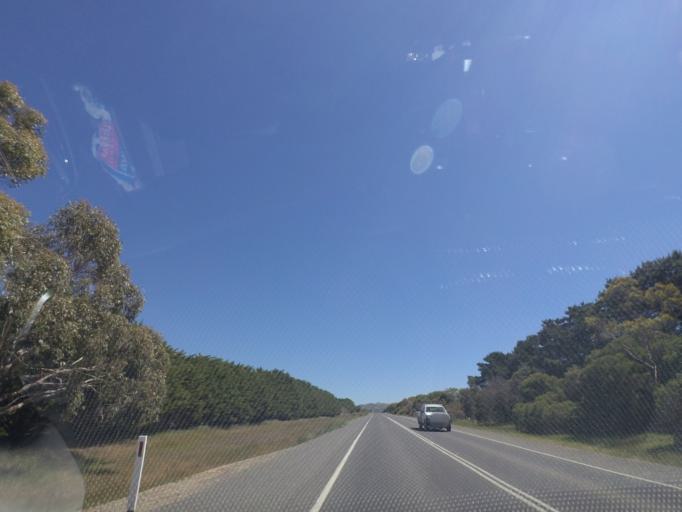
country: AU
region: Victoria
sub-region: Hume
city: Sunbury
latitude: -37.3100
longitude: 144.8446
